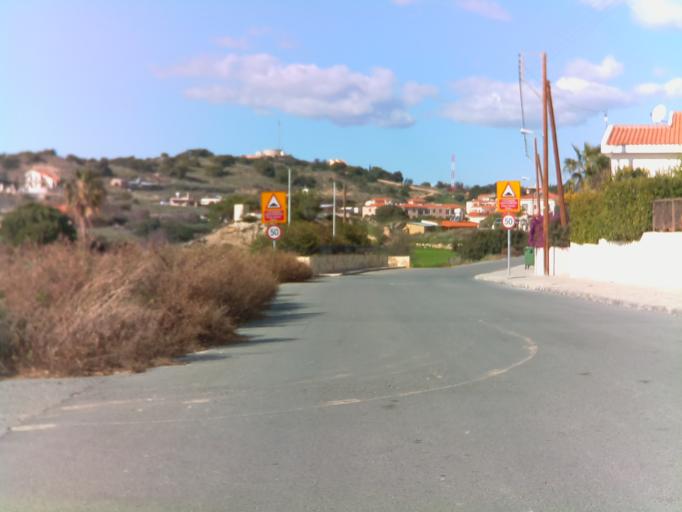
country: CY
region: Limassol
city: Pissouri
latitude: 34.6614
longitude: 32.6978
